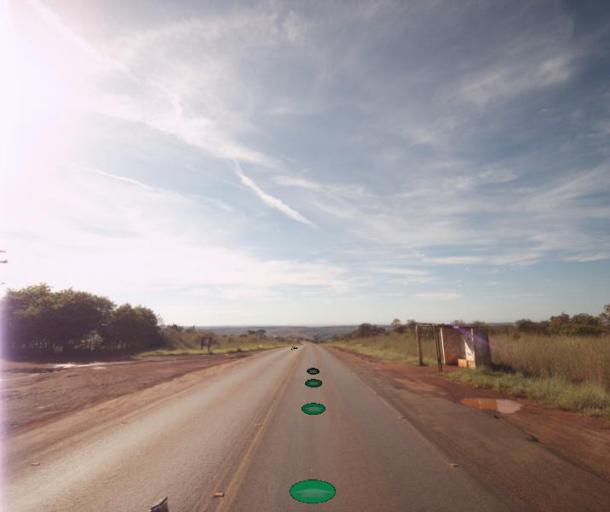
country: BR
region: Federal District
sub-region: Brasilia
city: Brasilia
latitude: -15.7398
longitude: -48.3853
